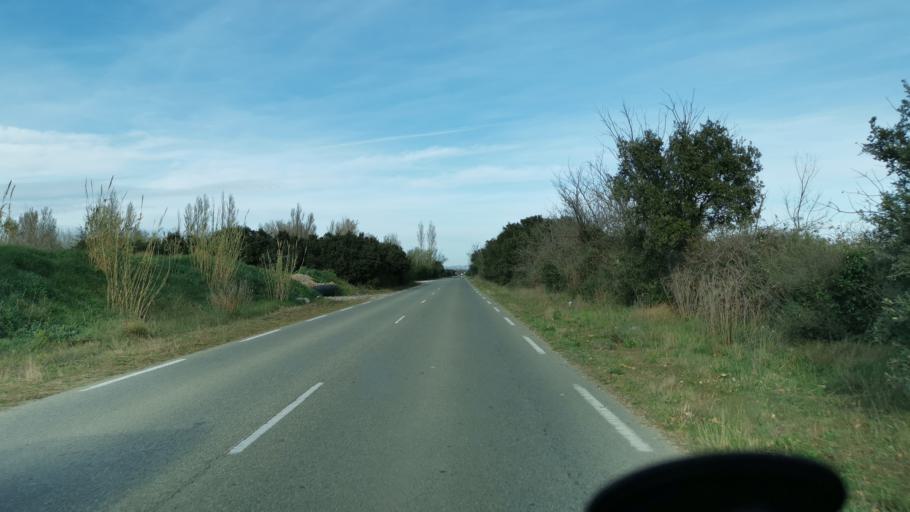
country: FR
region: Provence-Alpes-Cote d'Azur
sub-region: Departement des Bouches-du-Rhone
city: Saint-Martin-de-Crau
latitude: 43.5782
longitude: 4.7552
